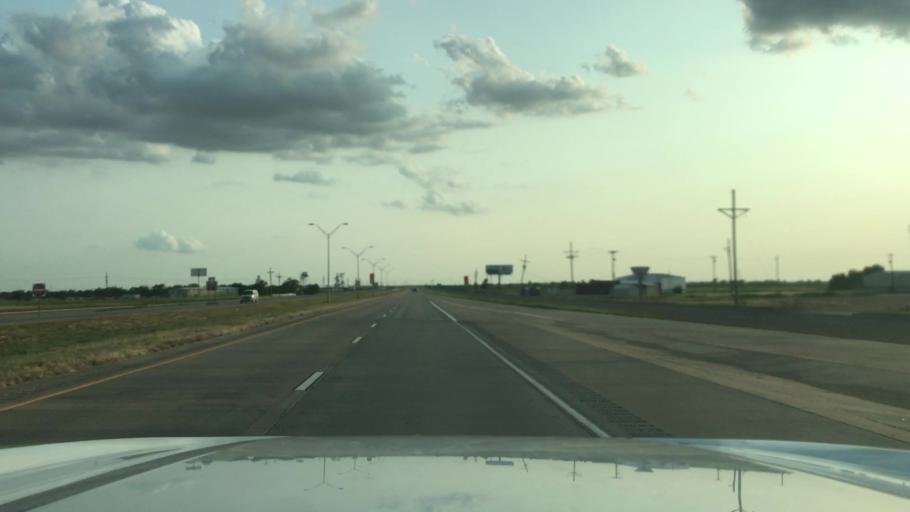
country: US
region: Texas
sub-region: Hale County
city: Seth Ward
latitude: 34.2304
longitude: -101.7127
